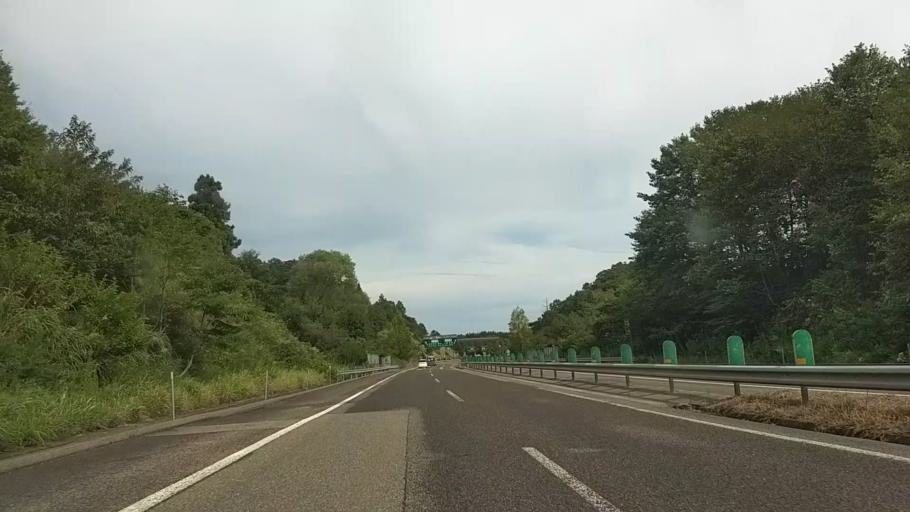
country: JP
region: Niigata
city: Joetsu
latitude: 37.1332
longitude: 138.2129
